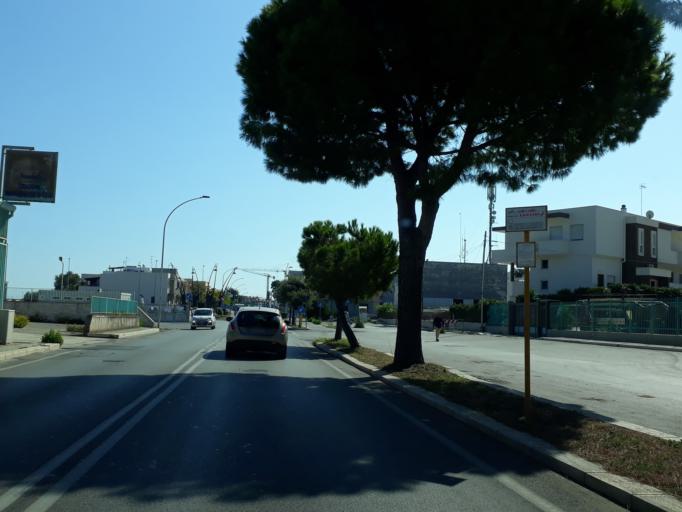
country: IT
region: Apulia
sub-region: Provincia di Bari
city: Monopoli
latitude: 40.9420
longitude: 17.3047
